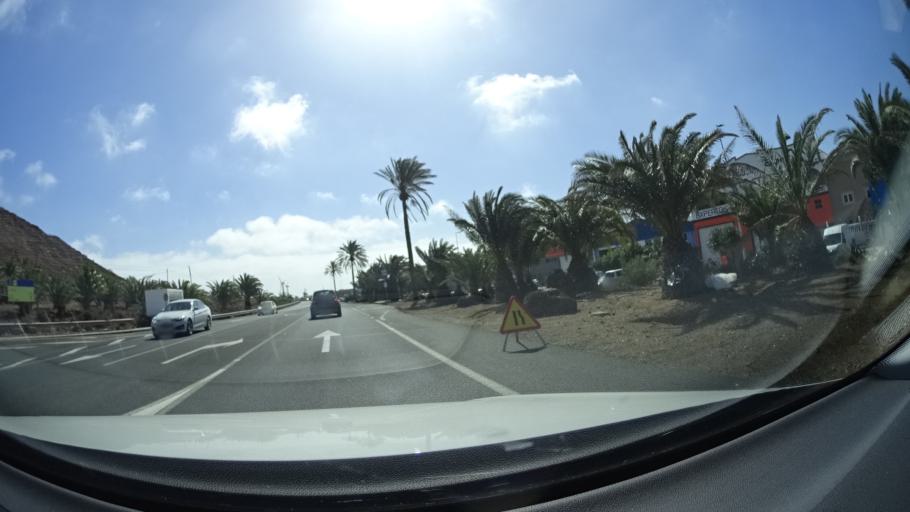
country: ES
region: Canary Islands
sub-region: Provincia de Las Palmas
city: Cruce de Arinaga
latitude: 27.8682
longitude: -15.4149
